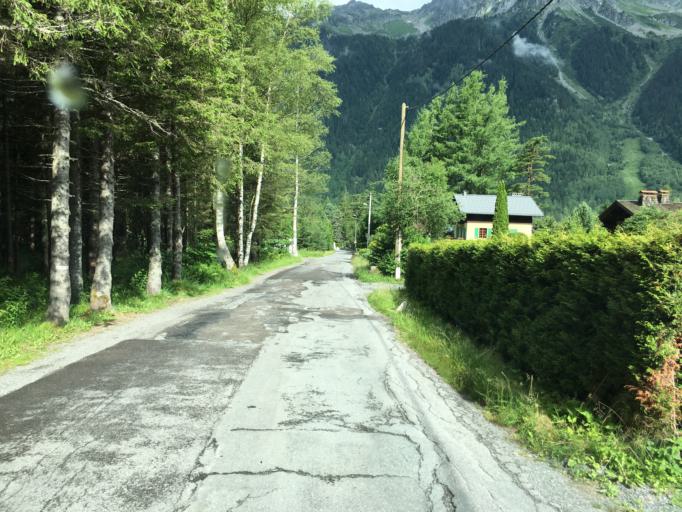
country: FR
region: Rhone-Alpes
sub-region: Departement de la Haute-Savoie
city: Chamonix-Mont-Blanc
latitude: 45.9399
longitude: 6.8945
